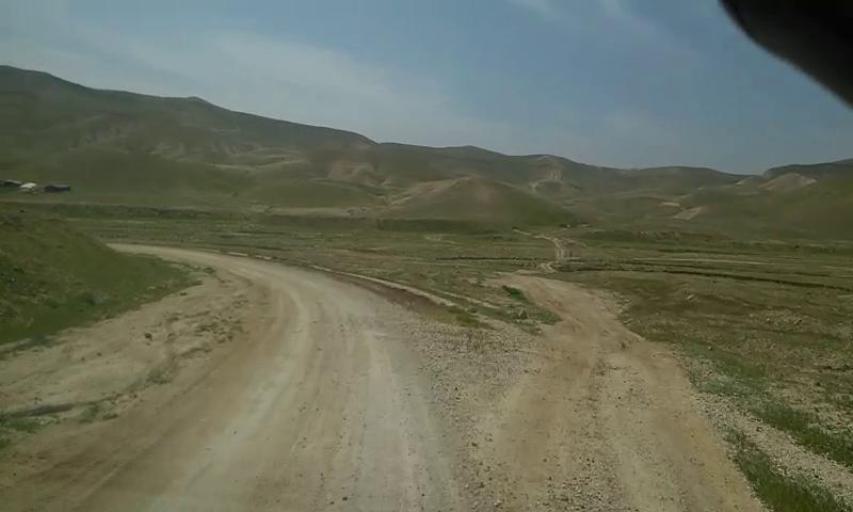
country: PS
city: `Arab ar Rashaydah
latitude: 31.5107
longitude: 35.2820
